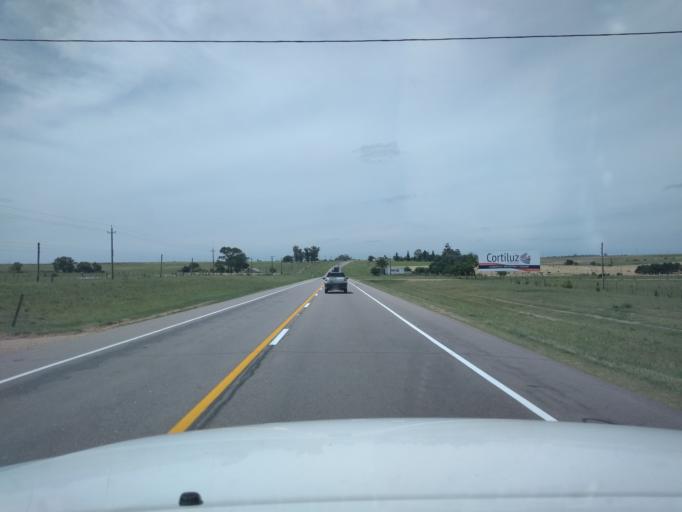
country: UY
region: Florida
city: Florida
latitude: -34.1749
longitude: -56.1895
